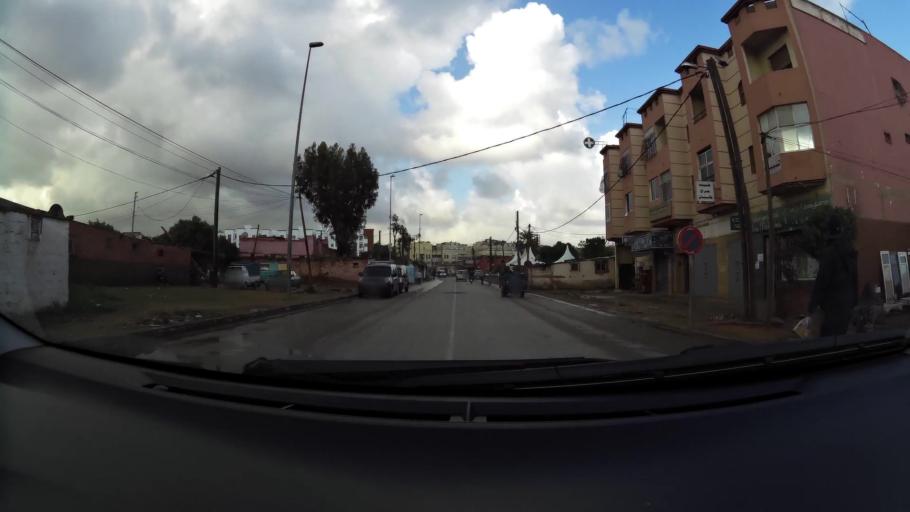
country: MA
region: Grand Casablanca
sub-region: Mediouna
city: Tit Mellil
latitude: 33.5821
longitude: -7.5334
